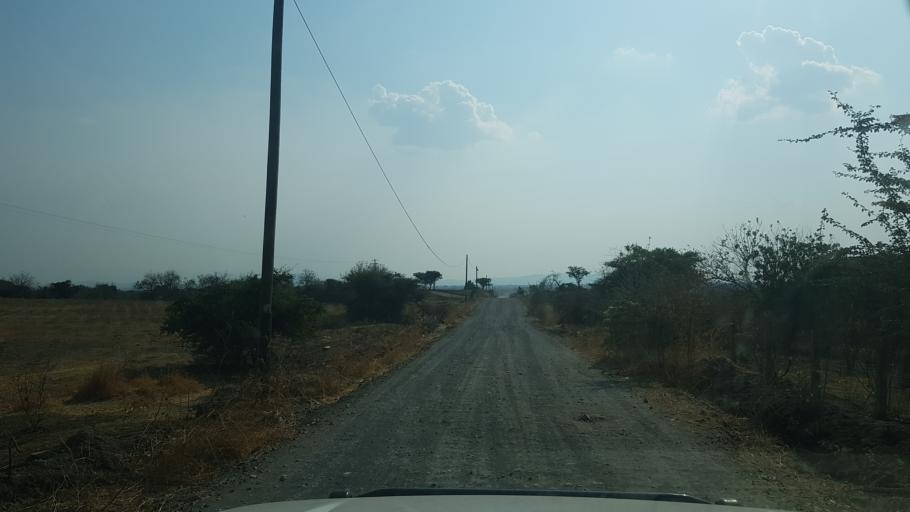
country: MX
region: Morelos
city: Tlacotepec
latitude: 18.7789
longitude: -98.7263
